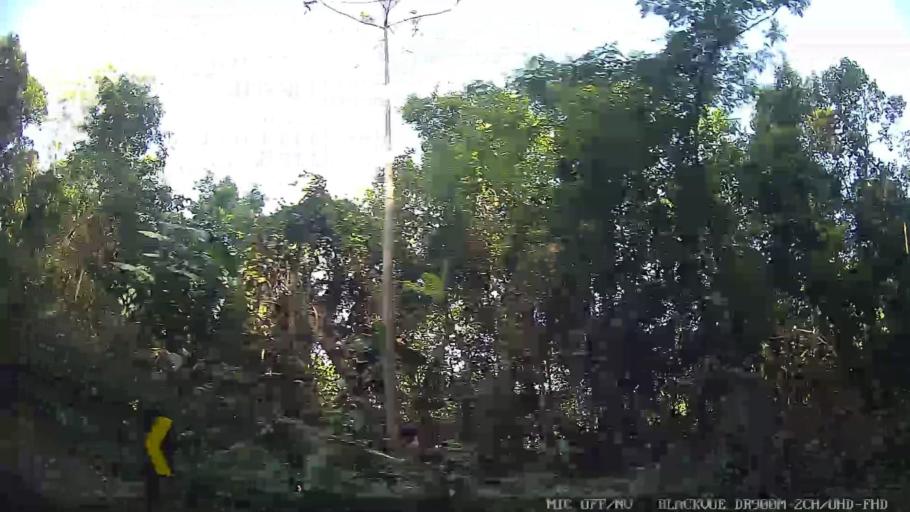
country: BR
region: Sao Paulo
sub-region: Cubatao
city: Cubatao
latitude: -23.8915
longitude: -46.4932
